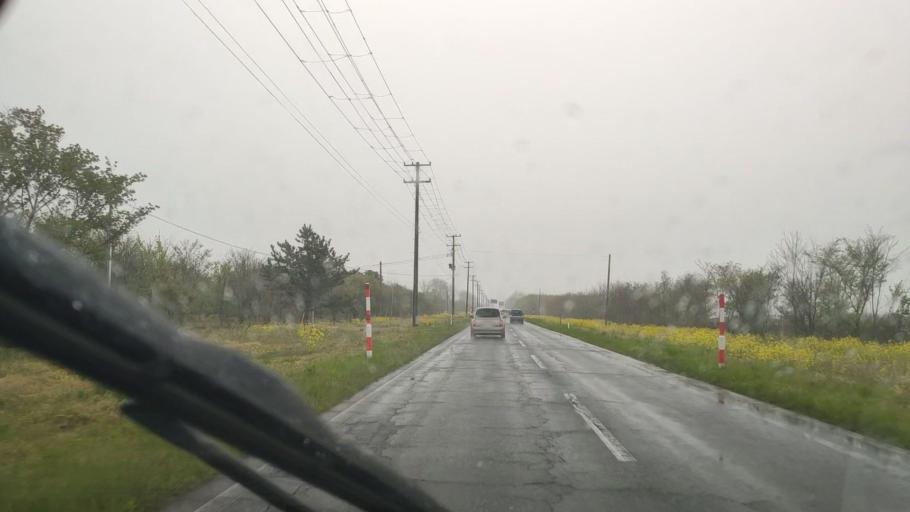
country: JP
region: Akita
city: Tenno
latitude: 39.9950
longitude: 139.9463
